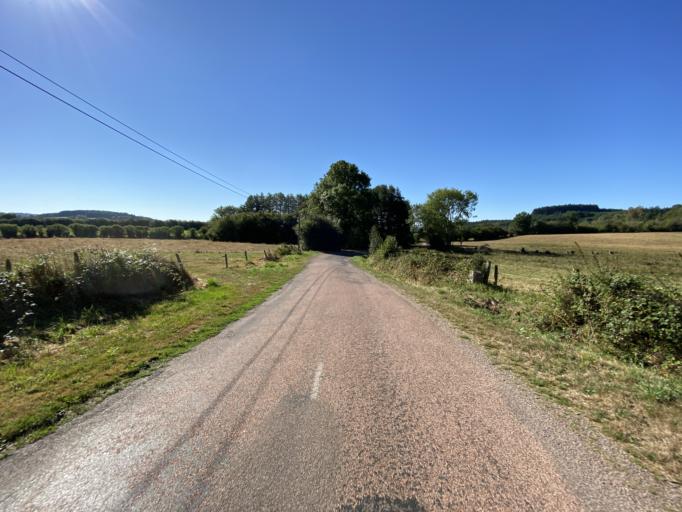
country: FR
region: Bourgogne
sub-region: Departement de la Cote-d'Or
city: Saulieu
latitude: 47.2683
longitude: 4.1744
